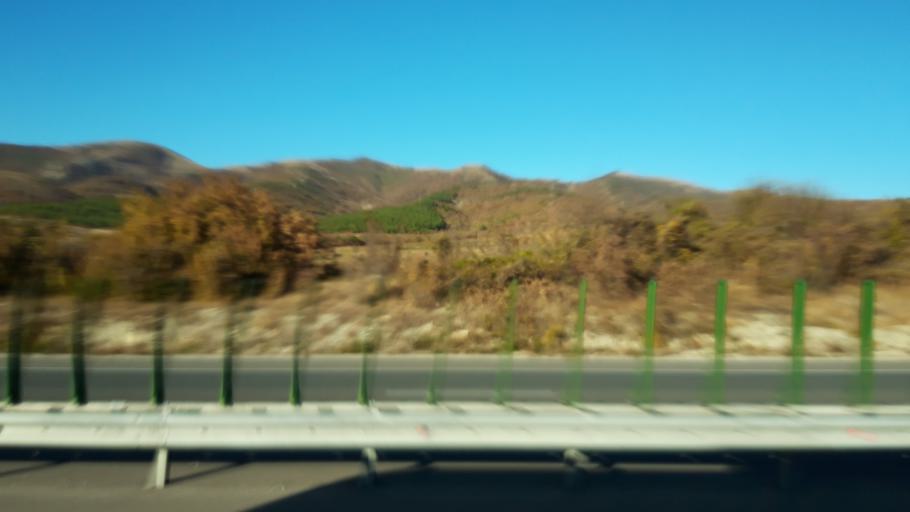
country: RU
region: Krasnodarskiy
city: Kabardinka
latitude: 44.6423
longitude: 37.9734
